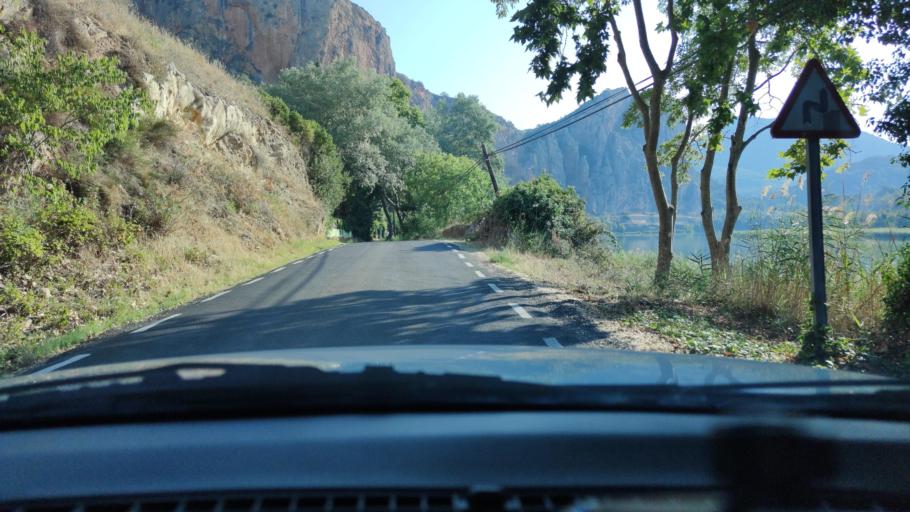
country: ES
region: Catalonia
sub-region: Provincia de Lleida
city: Camarasa
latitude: 41.8711
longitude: 0.8424
